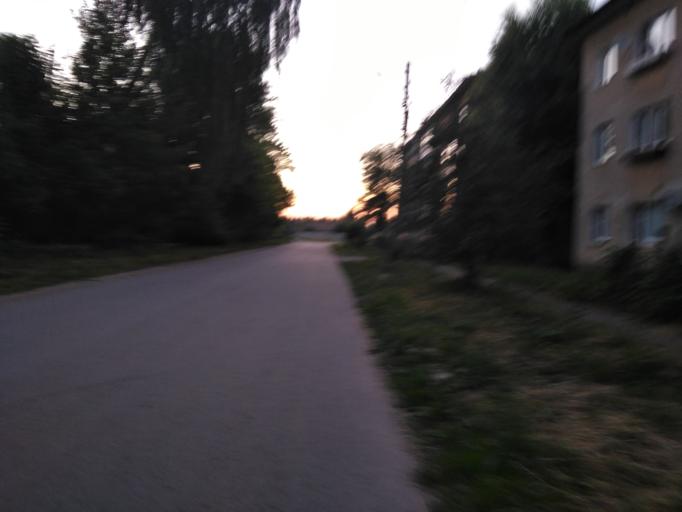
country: RU
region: Tula
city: Lomintsevskiy
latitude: 53.9374
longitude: 37.6271
